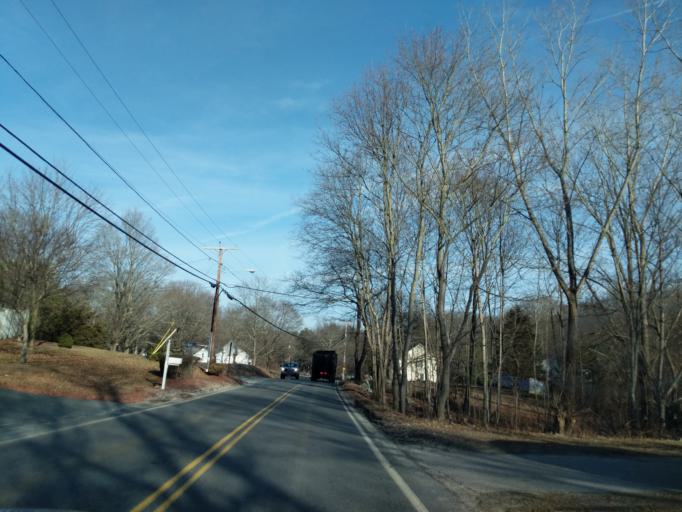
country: US
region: Massachusetts
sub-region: Worcester County
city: Blackstone
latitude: 42.0399
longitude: -71.5191
